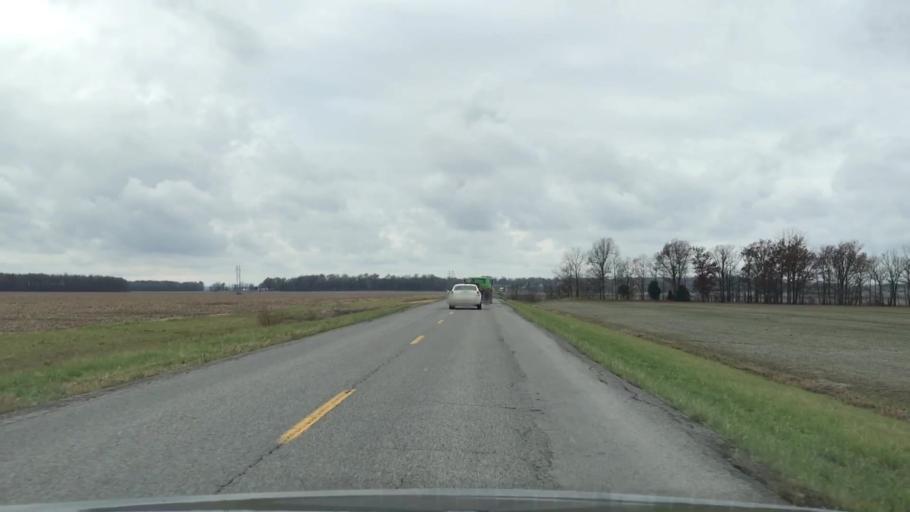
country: US
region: Kentucky
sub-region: McLean County
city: Calhoun
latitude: 37.5248
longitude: -87.3662
